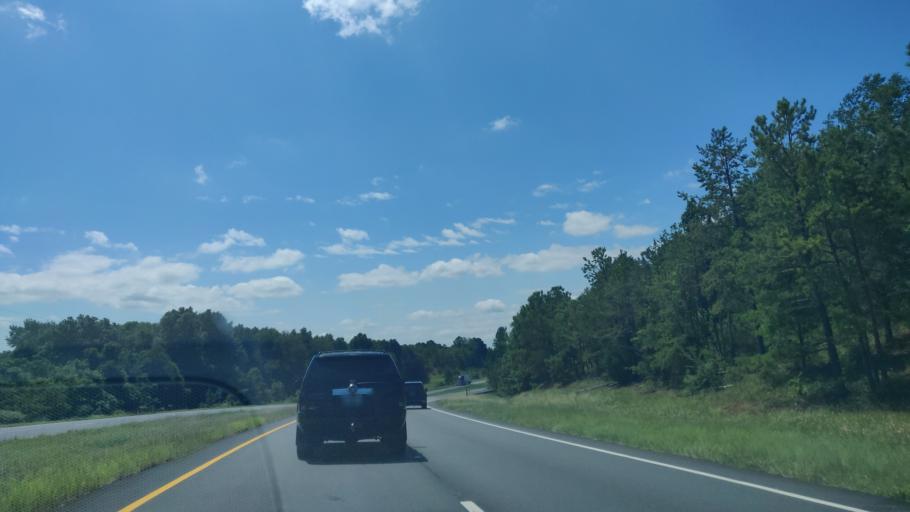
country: US
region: Georgia
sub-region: Stewart County
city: Richland
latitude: 32.1607
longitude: -84.6995
